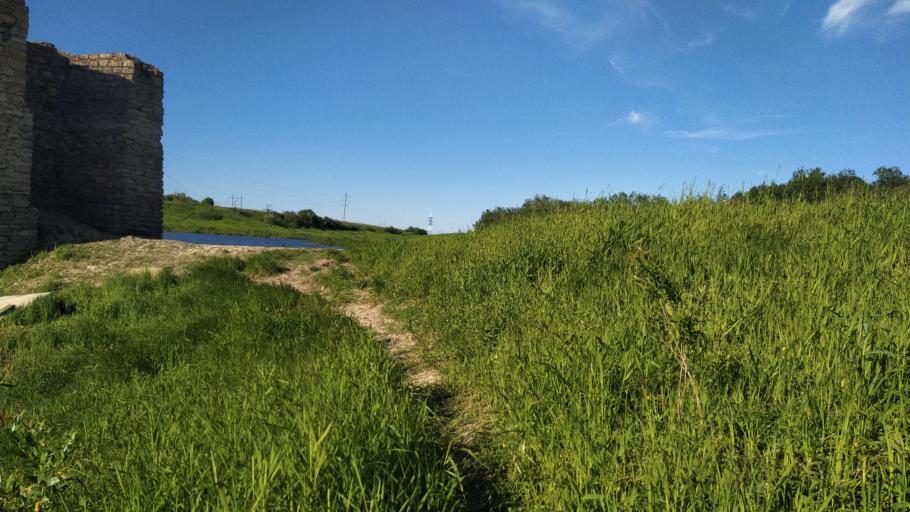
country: RU
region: St.-Petersburg
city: Aleksandrovskaya
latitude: 59.7424
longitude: 30.3688
